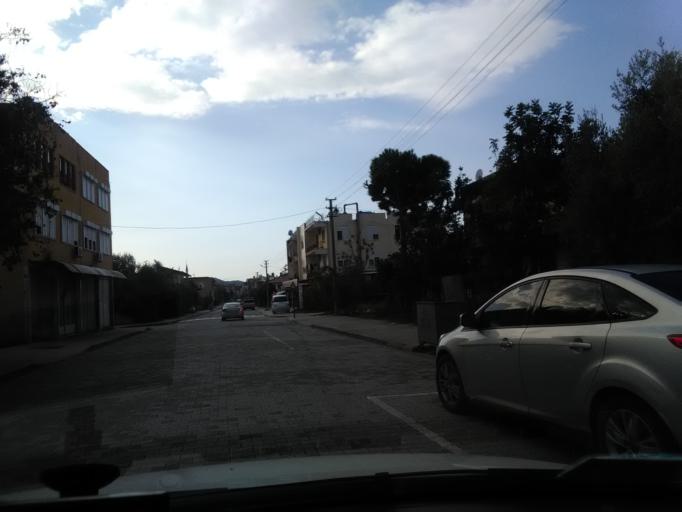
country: TR
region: Antalya
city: Gazipasa
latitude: 36.2705
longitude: 32.3286
